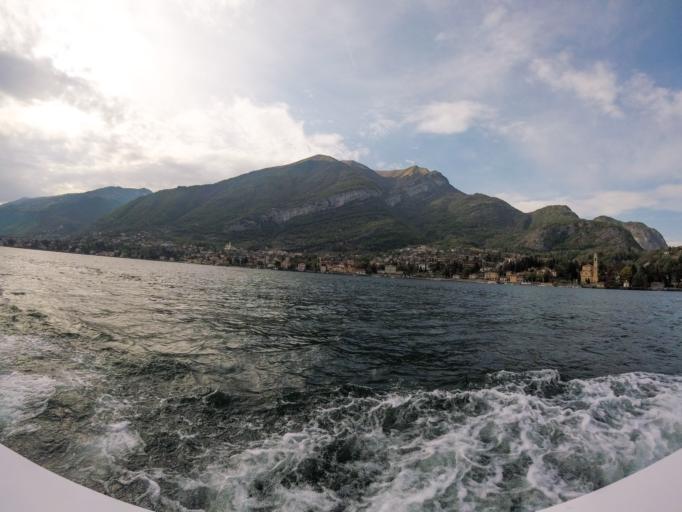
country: IT
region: Lombardy
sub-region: Provincia di Como
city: Tremezzo
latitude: 45.9775
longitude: 9.2195
